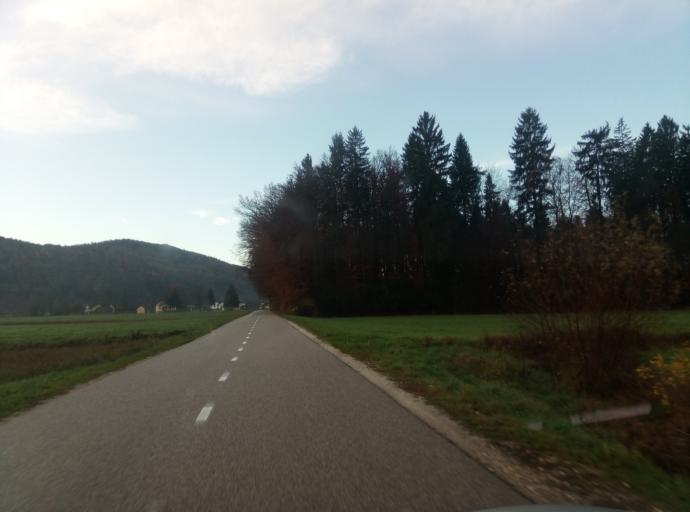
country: SI
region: Vodice
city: Vodice
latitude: 46.1665
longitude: 14.5186
